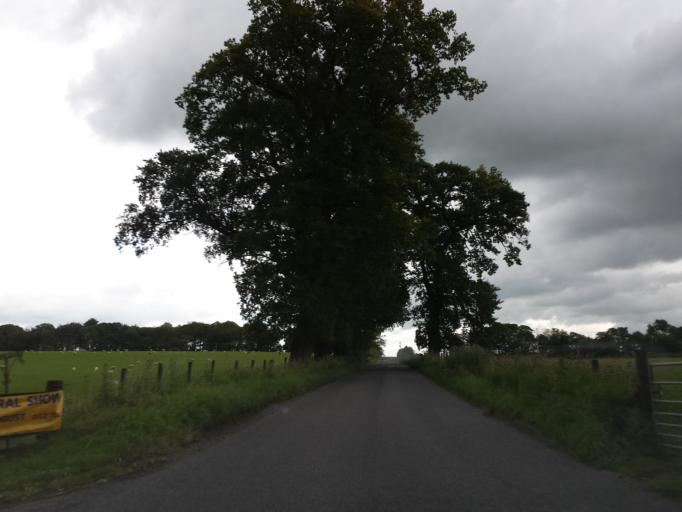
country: GB
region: Scotland
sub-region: Dumfries and Galloway
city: Dumfries
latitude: 55.0282
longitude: -3.6248
